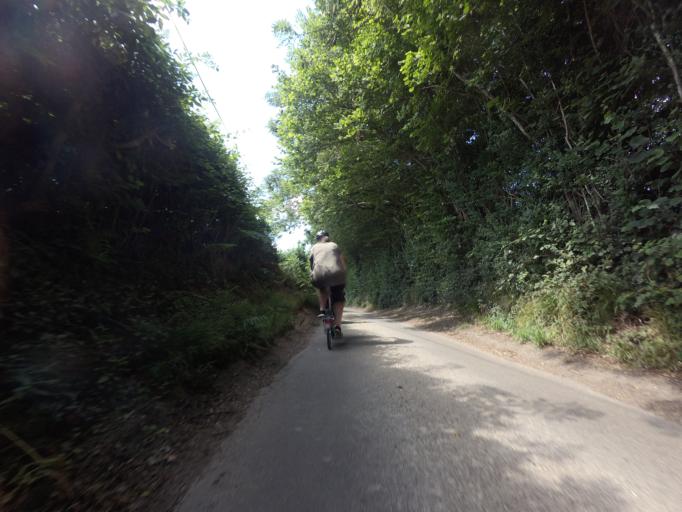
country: GB
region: England
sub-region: East Sussex
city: Horam
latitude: 50.9138
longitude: 0.2043
